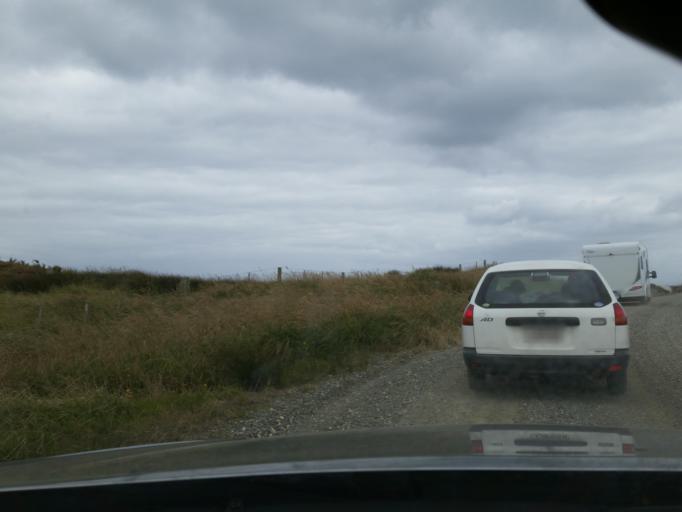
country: NZ
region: Southland
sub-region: Invercargill City
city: Bluff
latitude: -46.6589
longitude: 168.8528
